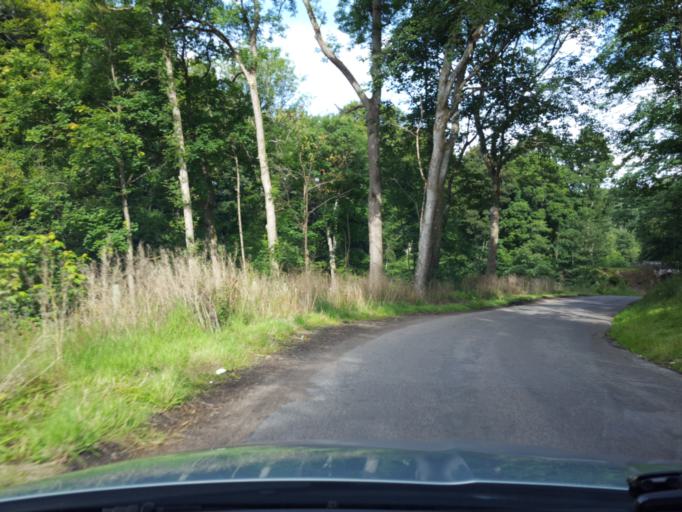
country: GB
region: Scotland
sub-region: Moray
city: Rothes
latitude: 57.4781
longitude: -3.1994
